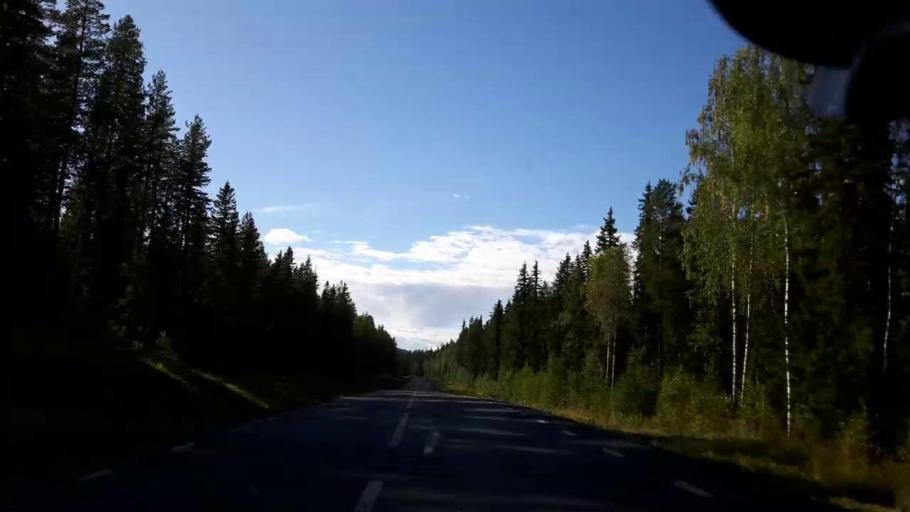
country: SE
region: Jaemtland
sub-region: Ragunda Kommun
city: Hammarstrand
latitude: 63.5364
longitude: 16.0344
